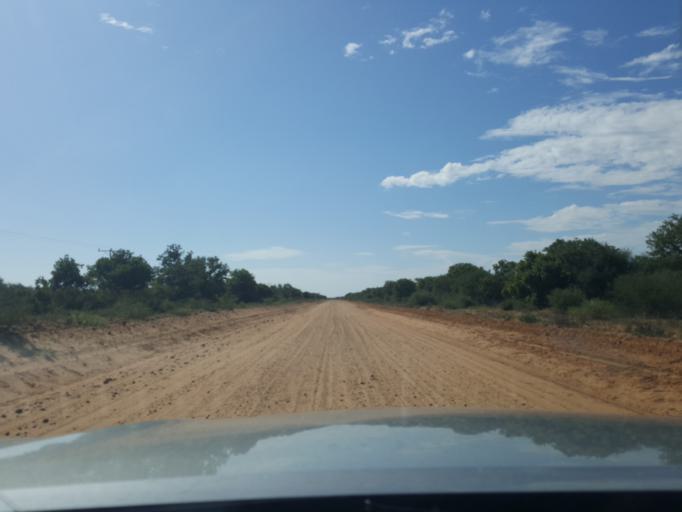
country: BW
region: Kweneng
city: Khudumelapye
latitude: -23.7218
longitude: 24.7380
